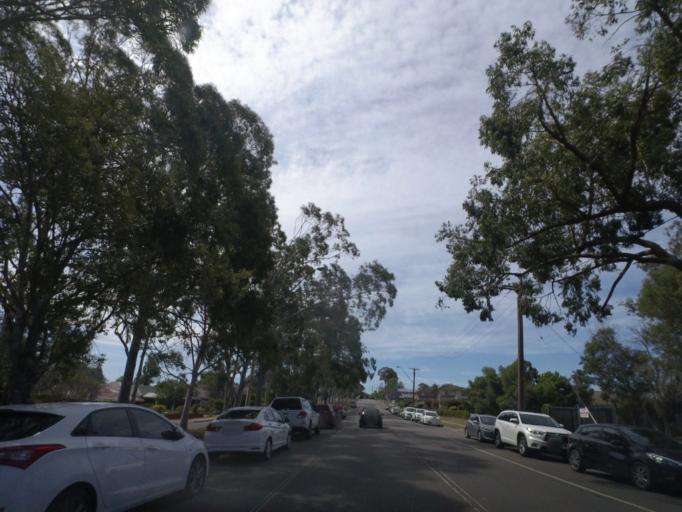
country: AU
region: New South Wales
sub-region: Camden
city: Camden South
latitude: -34.0699
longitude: 150.6942
